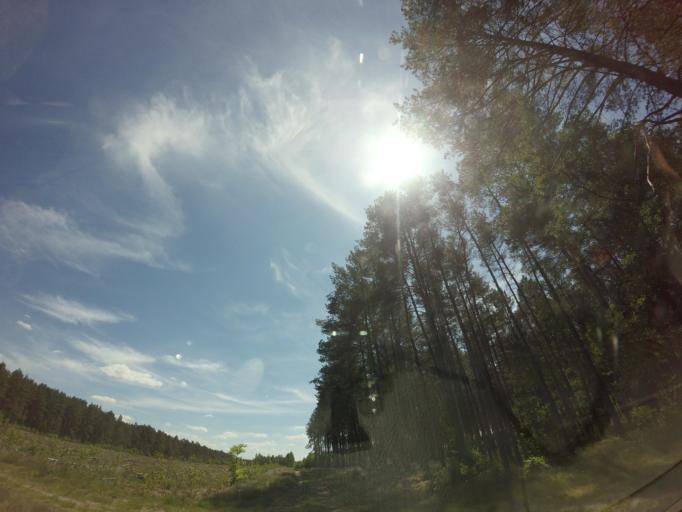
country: PL
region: West Pomeranian Voivodeship
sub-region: Powiat drawski
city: Kalisz Pomorski
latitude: 53.1743
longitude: 15.9023
